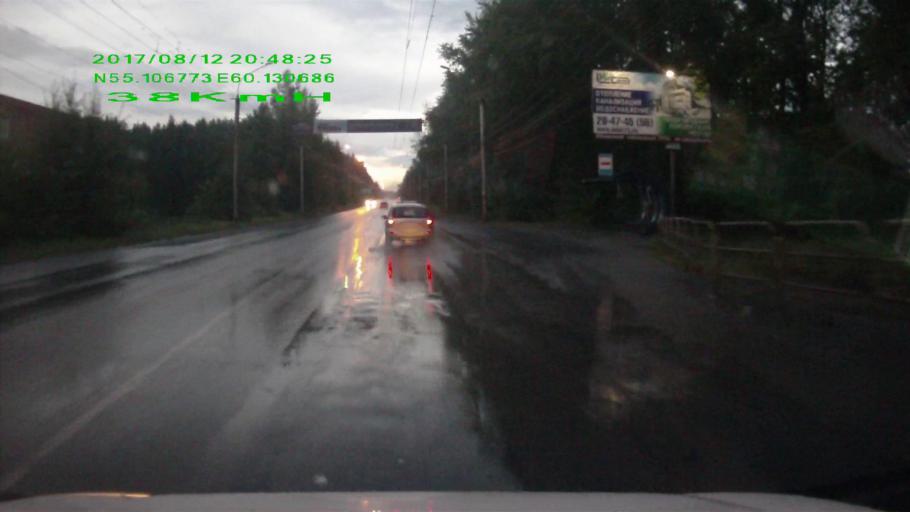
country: RU
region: Chelyabinsk
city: Turgoyak
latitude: 55.1069
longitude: 60.1307
